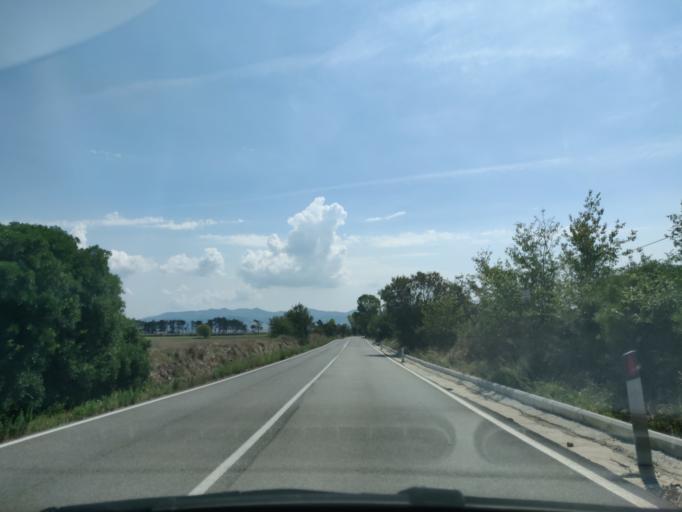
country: IT
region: Latium
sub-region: Provincia di Viterbo
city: Tarquinia
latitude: 42.2316
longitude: 11.7956
